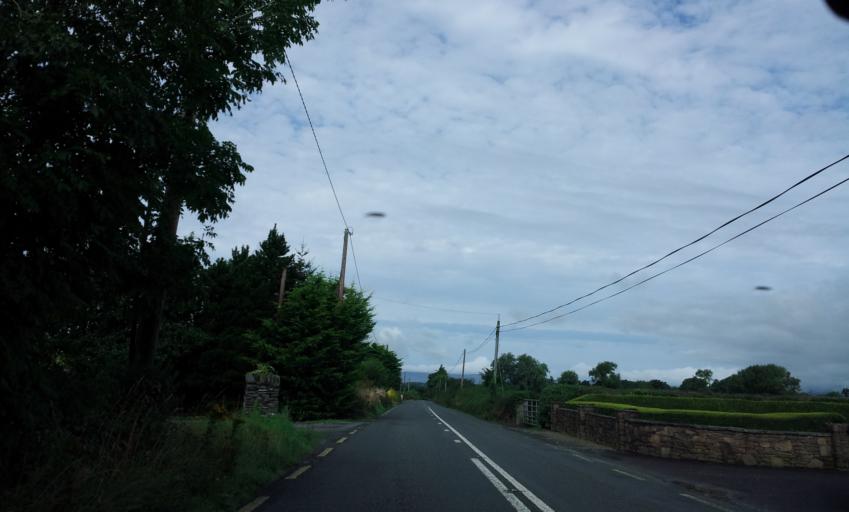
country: IE
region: Munster
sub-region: Ciarrai
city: Killorglin
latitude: 52.0834
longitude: -9.6727
